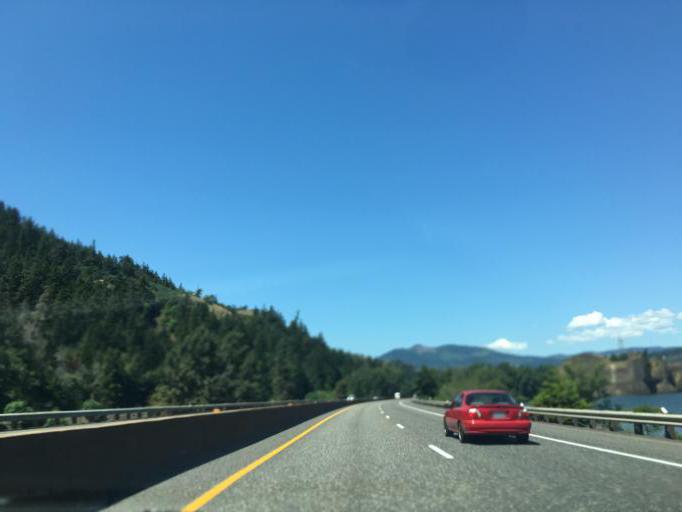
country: US
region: Washington
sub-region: Klickitat County
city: White Salmon
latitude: 45.6991
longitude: -121.4675
